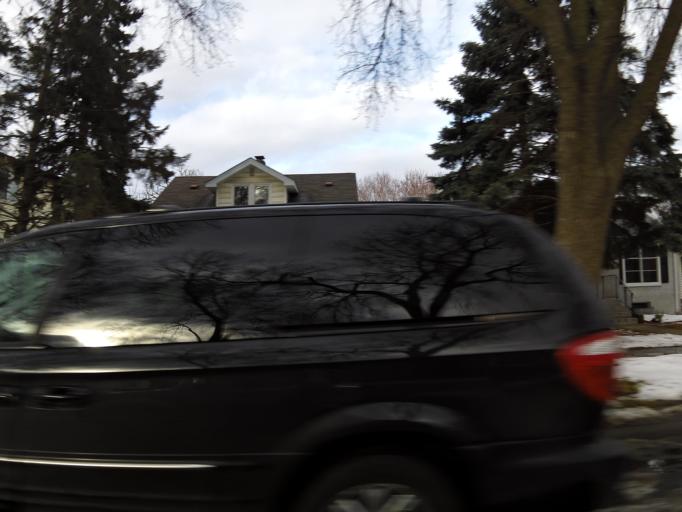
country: US
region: Minnesota
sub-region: Ramsey County
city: Falcon Heights
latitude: 44.9503
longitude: -93.1628
